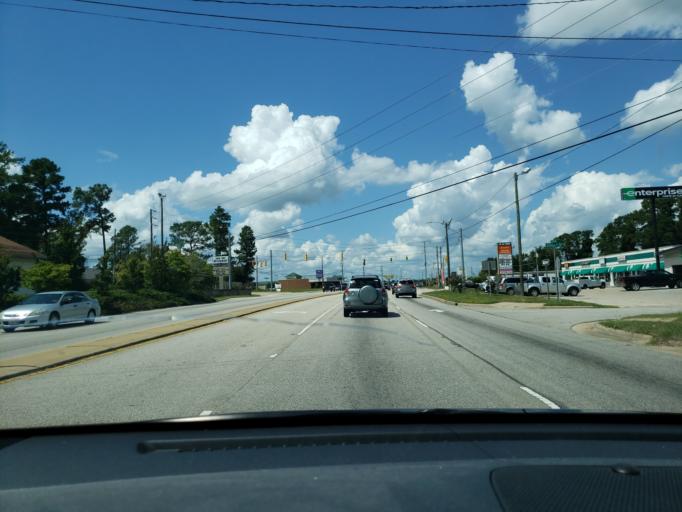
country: US
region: North Carolina
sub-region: Cumberland County
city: Spring Lake
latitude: 35.1765
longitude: -78.9793
